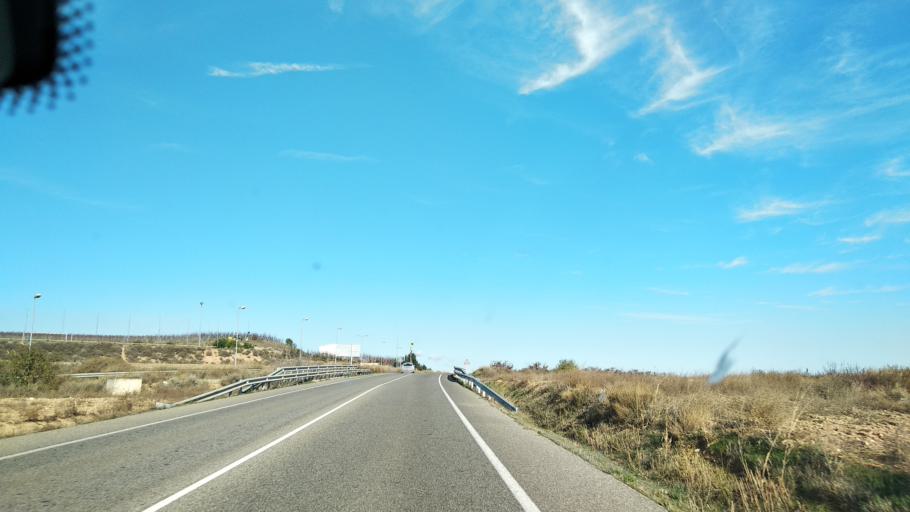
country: ES
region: Catalonia
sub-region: Provincia de Lleida
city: Corbins
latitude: 41.7048
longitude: 0.7113
